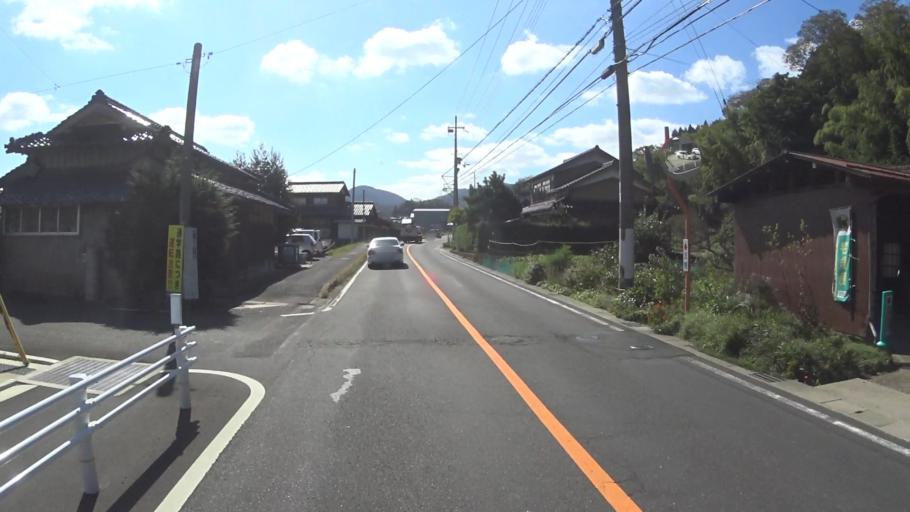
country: JP
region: Kyoto
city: Miyazu
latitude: 35.6558
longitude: 135.0326
